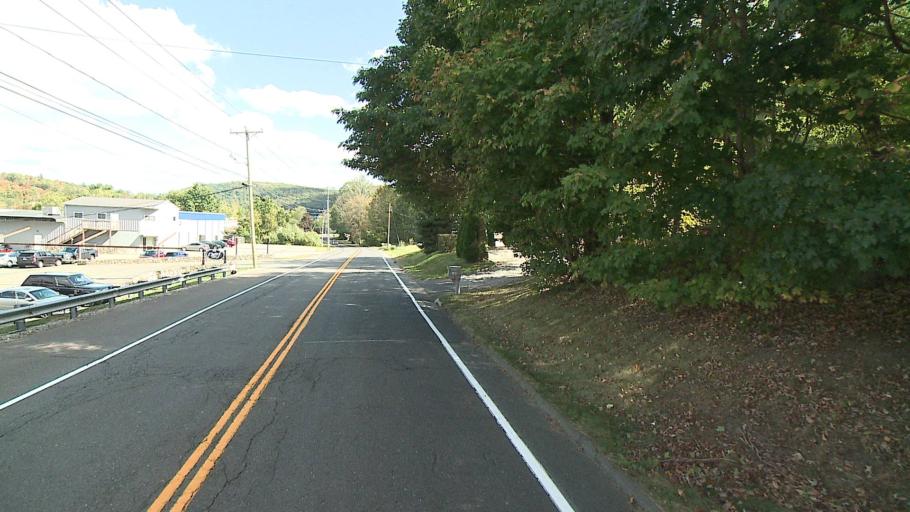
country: US
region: Connecticut
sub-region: New Haven County
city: Seymour
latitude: 41.4276
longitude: -73.0819
